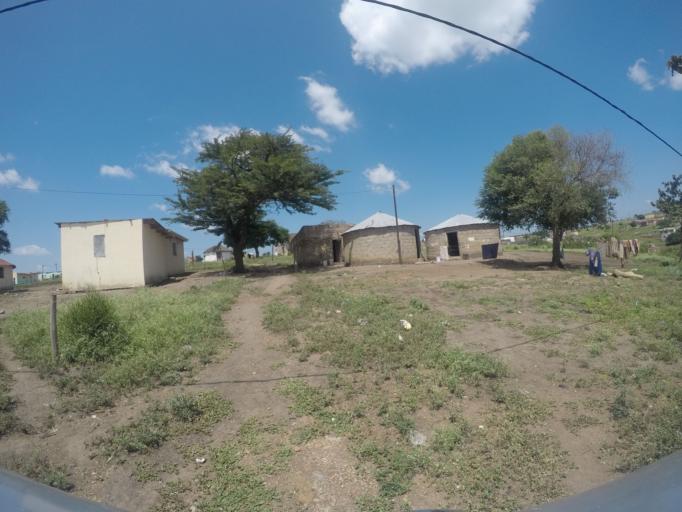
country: ZA
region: KwaZulu-Natal
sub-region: uThungulu District Municipality
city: Empangeni
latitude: -28.6088
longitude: 31.7361
